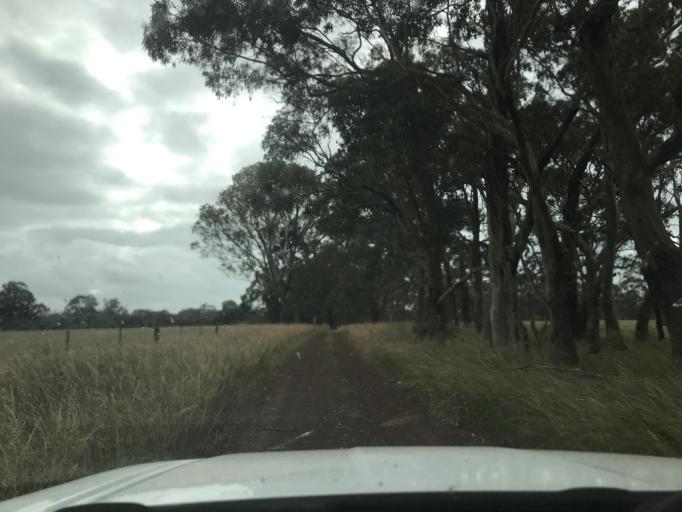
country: AU
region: South Australia
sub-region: Wattle Range
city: Penola
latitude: -37.1156
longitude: 141.0735
